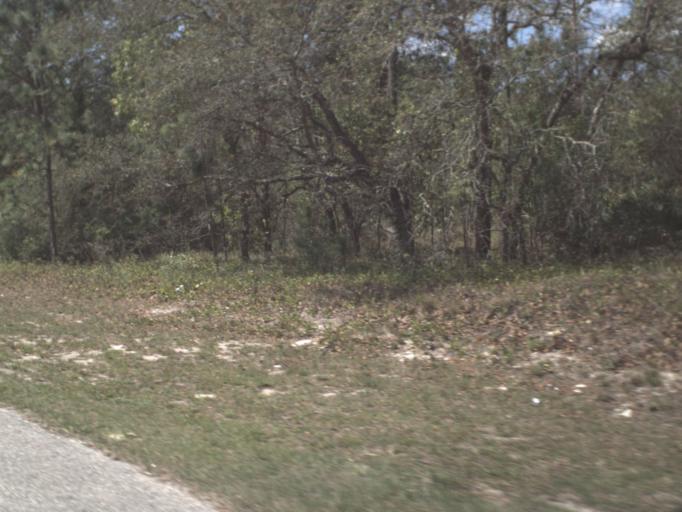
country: US
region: Florida
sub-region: Flagler County
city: Palm Coast
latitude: 29.6346
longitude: -81.2845
